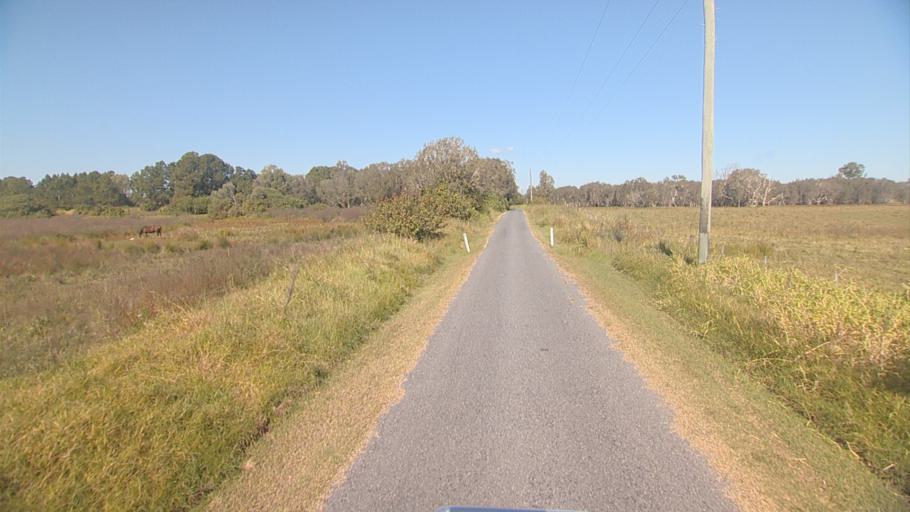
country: AU
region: Queensland
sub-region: Gold Coast
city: Yatala
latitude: -27.6835
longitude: 153.2251
